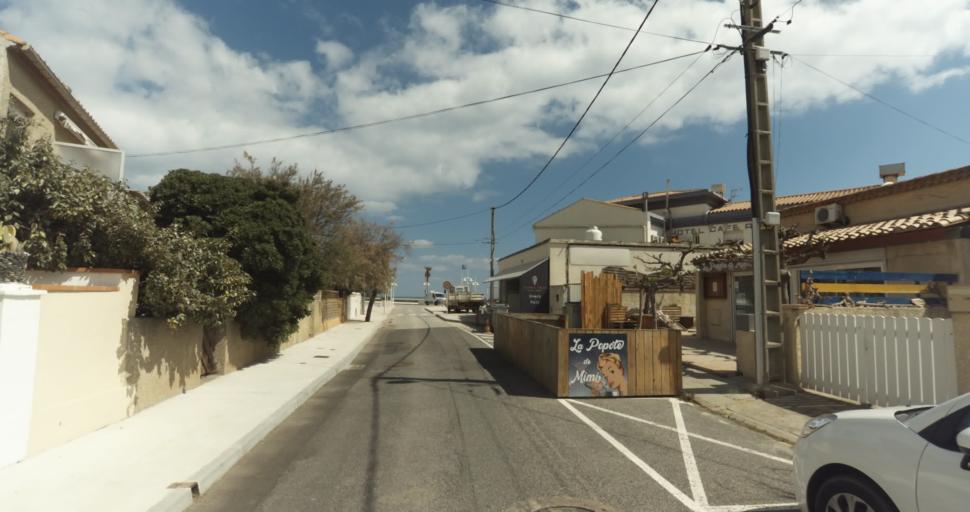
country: FR
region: Languedoc-Roussillon
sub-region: Departement de l'Aude
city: Leucate
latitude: 42.9049
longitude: 3.0551
